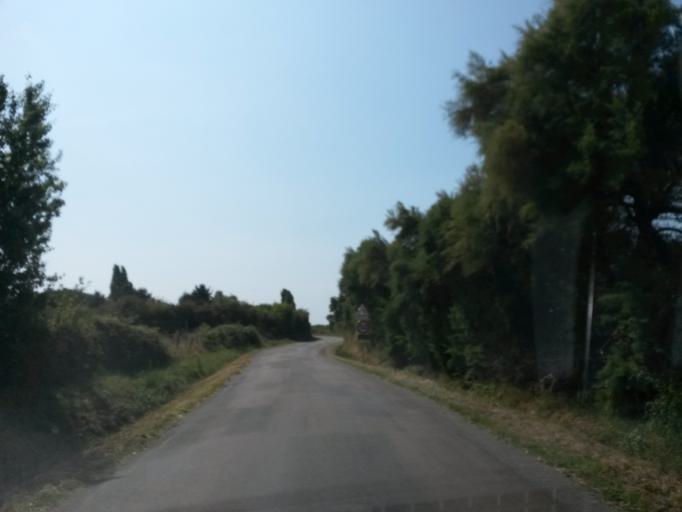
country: FR
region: Pays de la Loire
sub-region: Departement de la Vendee
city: Saint-Hilaire-de-Talmont
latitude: 46.4388
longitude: -1.6025
